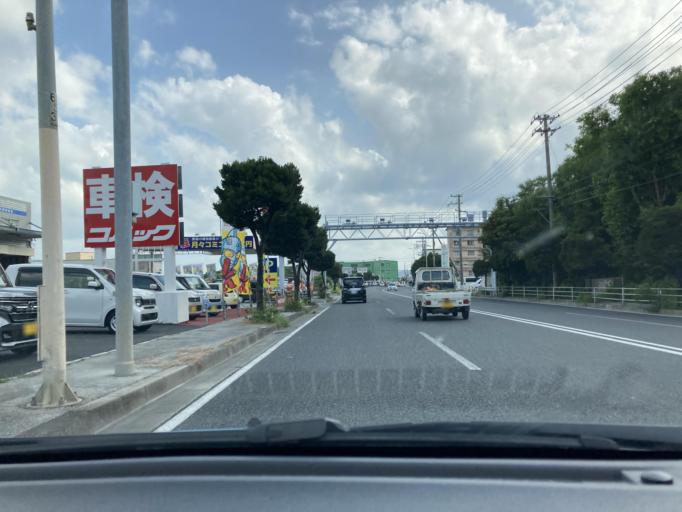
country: JP
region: Okinawa
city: Ginowan
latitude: 26.2351
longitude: 127.7697
